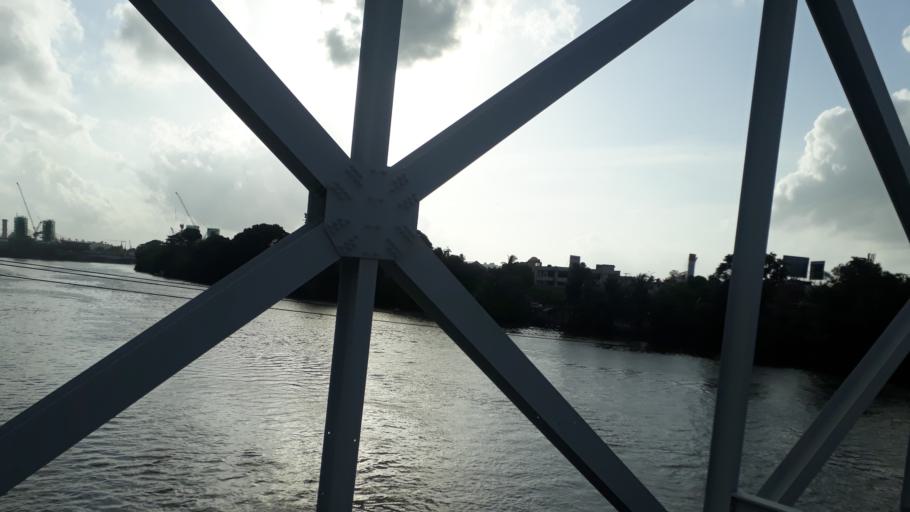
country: LK
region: Western
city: Peliyagoda
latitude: 6.9541
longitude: 79.8896
